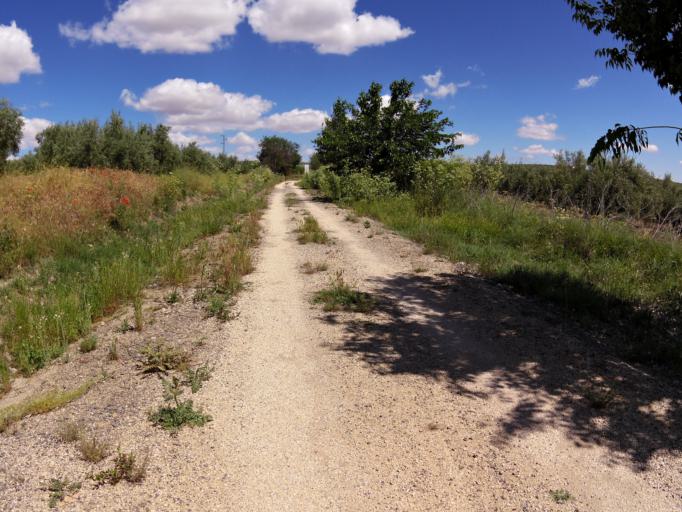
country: ES
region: Andalusia
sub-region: Provincia de Jaen
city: Alcaudete
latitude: 37.6595
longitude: -4.0625
